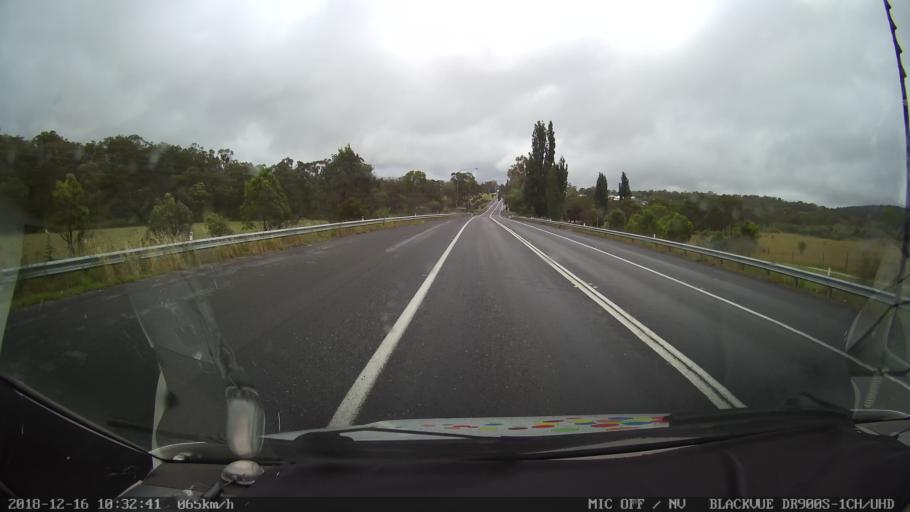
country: AU
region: New South Wales
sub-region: Tenterfield Municipality
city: Carrolls Creek
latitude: -29.0701
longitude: 152.0129
